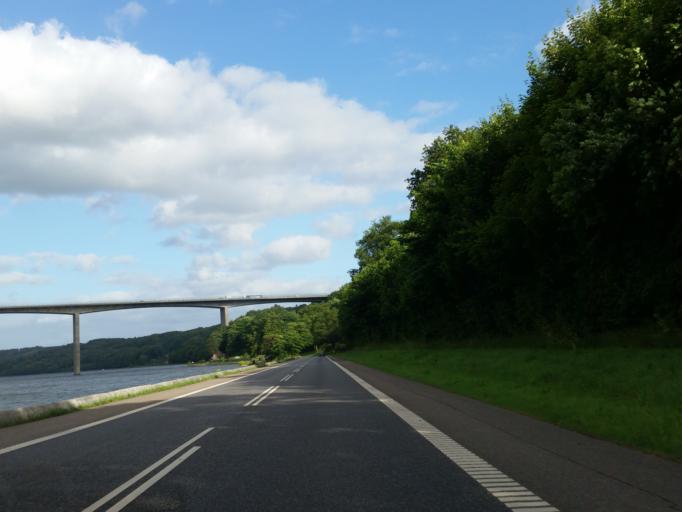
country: DK
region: South Denmark
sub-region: Vejle Kommune
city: Vejle
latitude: 55.6963
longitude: 9.5624
